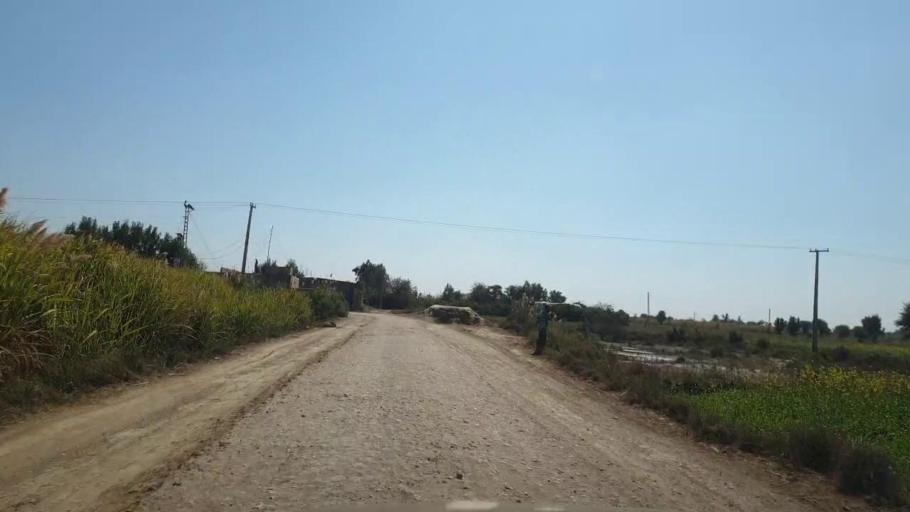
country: PK
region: Sindh
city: Mirpur Khas
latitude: 25.5942
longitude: 69.1051
